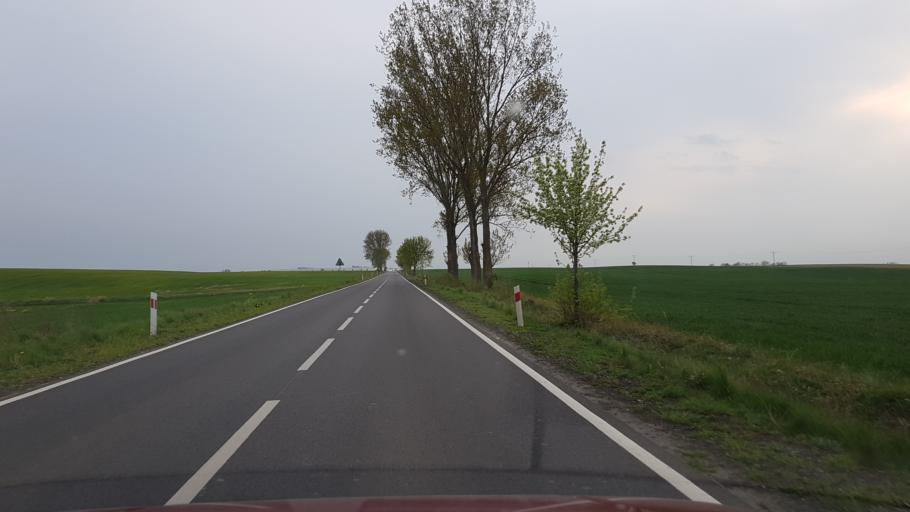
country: PL
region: West Pomeranian Voivodeship
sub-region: Powiat pyrzycki
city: Bielice
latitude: 53.2721
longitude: 14.6588
